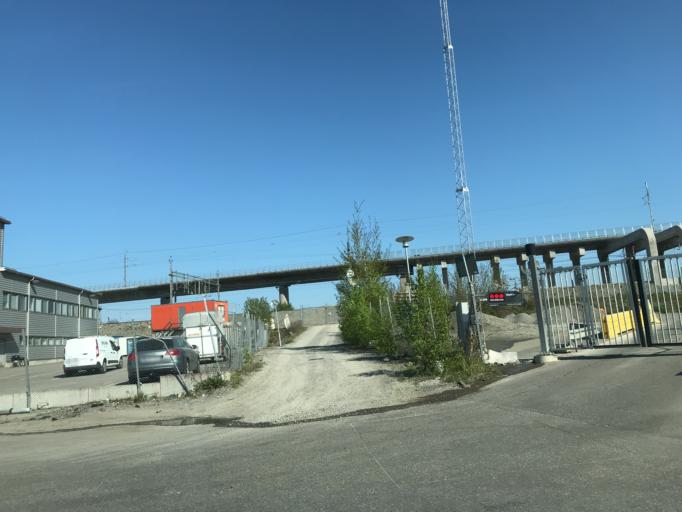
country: SE
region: Stockholm
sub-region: Stockholms Kommun
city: Arsta
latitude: 59.2952
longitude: 18.0193
